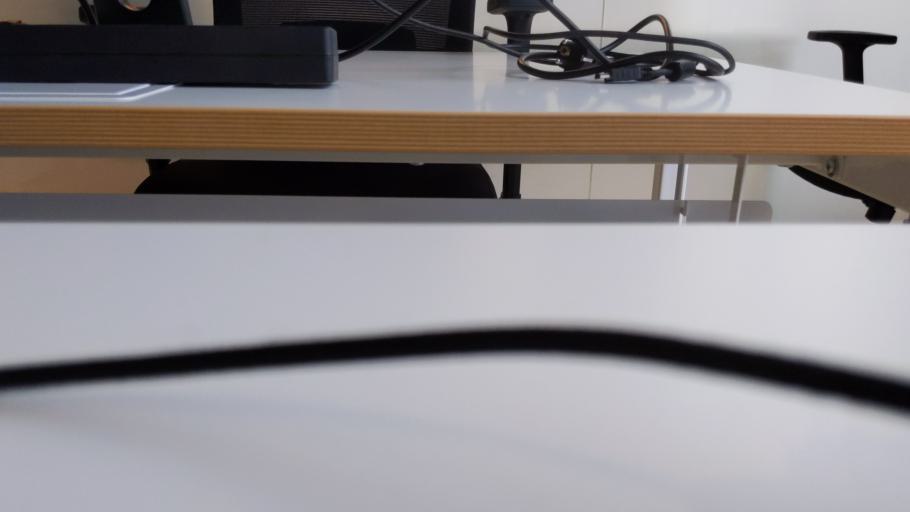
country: RU
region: Moskovskaya
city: Shevlyakovo
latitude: 56.4055
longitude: 36.8935
